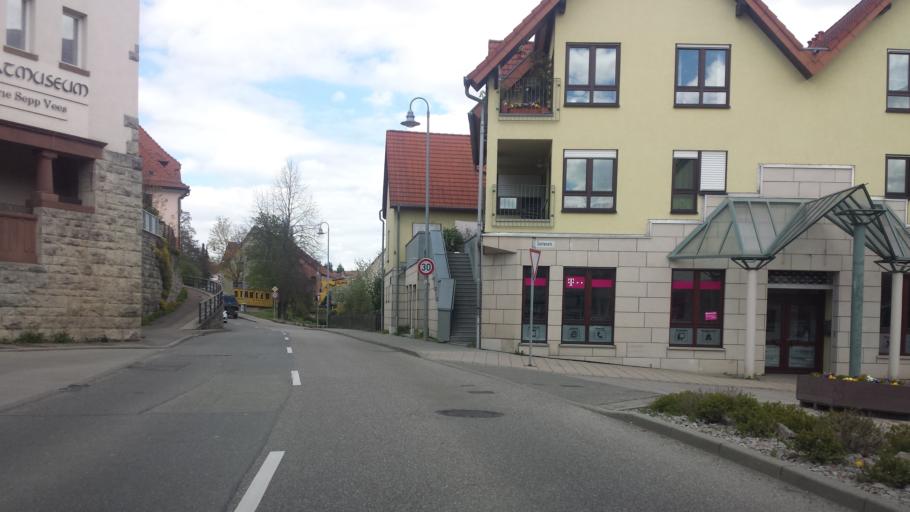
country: DE
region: Baden-Wuerttemberg
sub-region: Regierungsbezirk Stuttgart
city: Weissach
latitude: 48.8339
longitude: 8.9132
